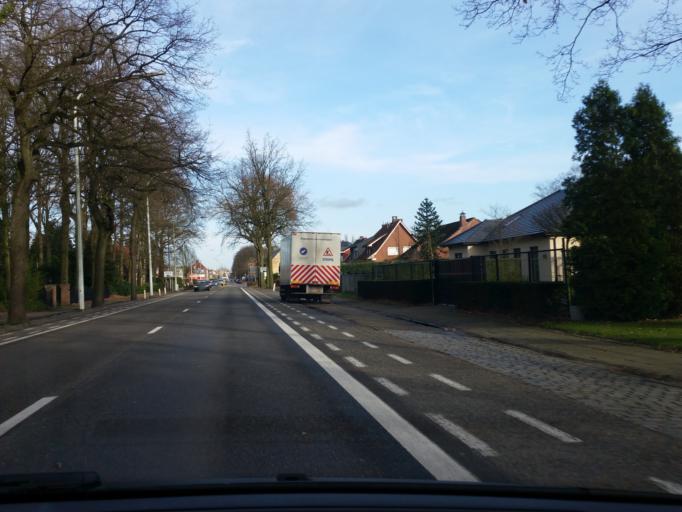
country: BE
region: Flanders
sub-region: Provincie Antwerpen
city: Wuustwezel
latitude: 51.3491
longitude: 4.5415
